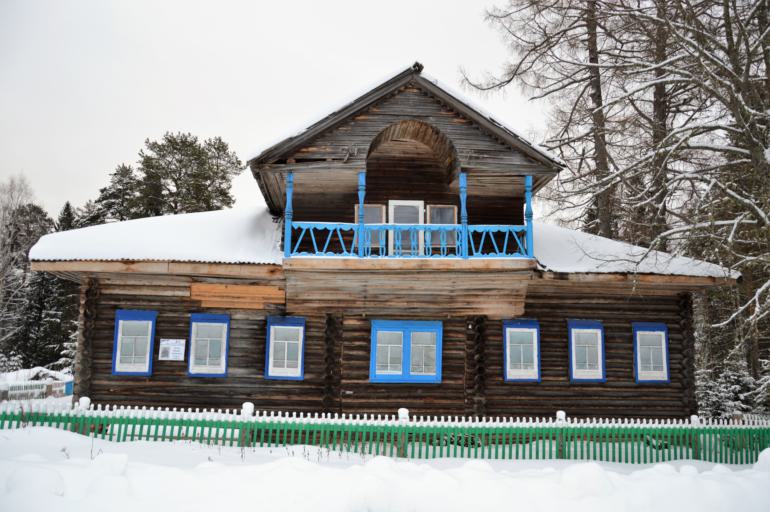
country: RU
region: Kirov
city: Maromitsa
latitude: 59.3617
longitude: 47.8844
